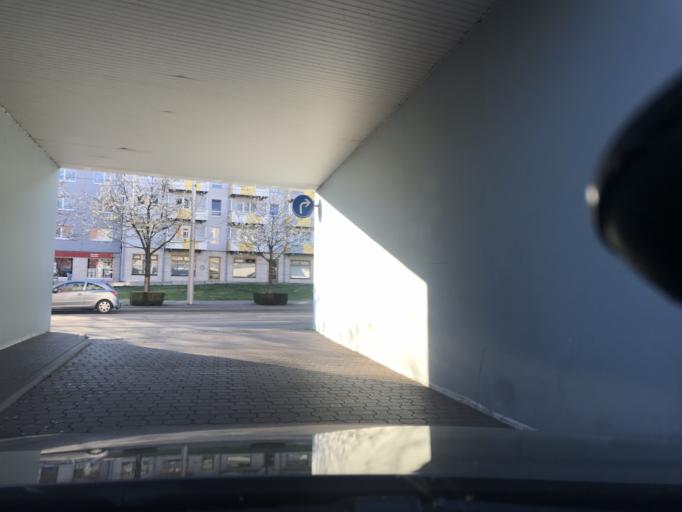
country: DE
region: Thuringia
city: Nordhausen
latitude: 51.4972
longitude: 10.7927
